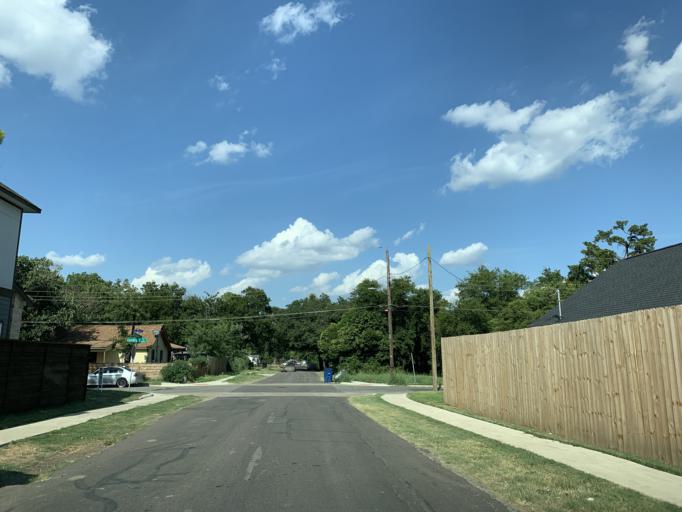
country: US
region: Texas
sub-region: Dallas County
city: Dallas
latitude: 32.7023
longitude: -96.7805
